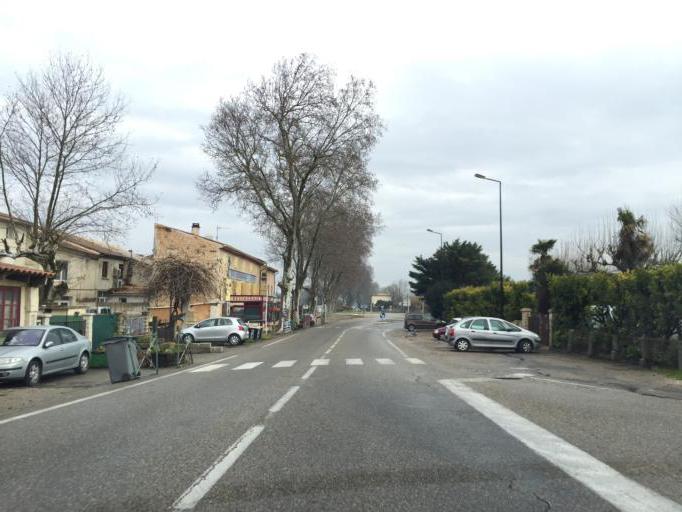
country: FR
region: Languedoc-Roussillon
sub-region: Departement du Gard
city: Pont-Saint-Esprit
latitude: 44.2609
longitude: 4.6610
